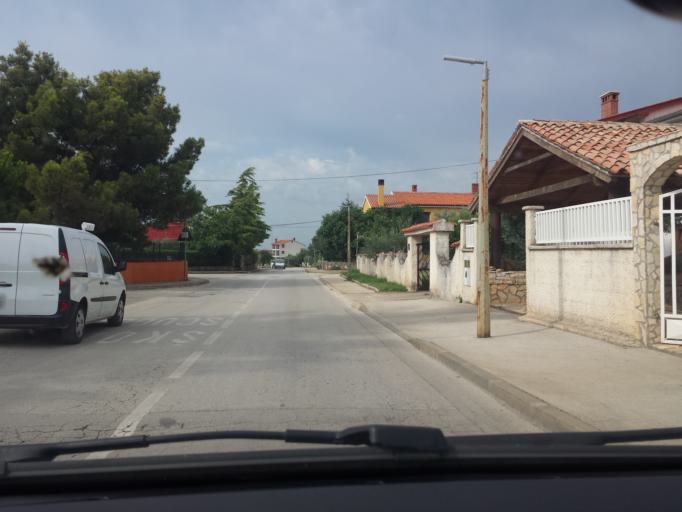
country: HR
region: Istarska
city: Galizana
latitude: 44.9301
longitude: 13.8685
